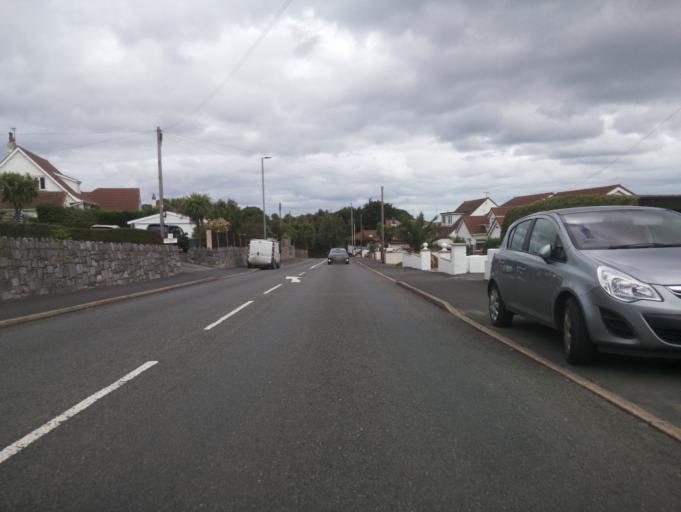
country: GB
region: England
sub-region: Devon
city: Teignmouth
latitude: 50.5605
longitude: -3.4799
